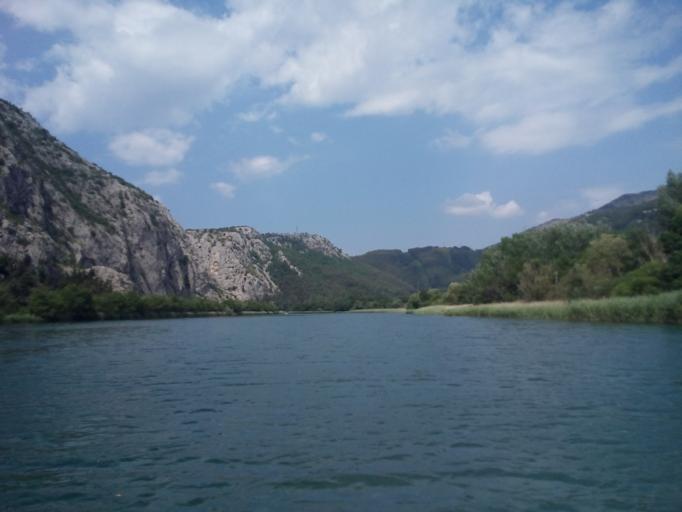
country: HR
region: Splitsko-Dalmatinska
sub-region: Grad Omis
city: Omis
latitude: 43.4503
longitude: 16.7095
